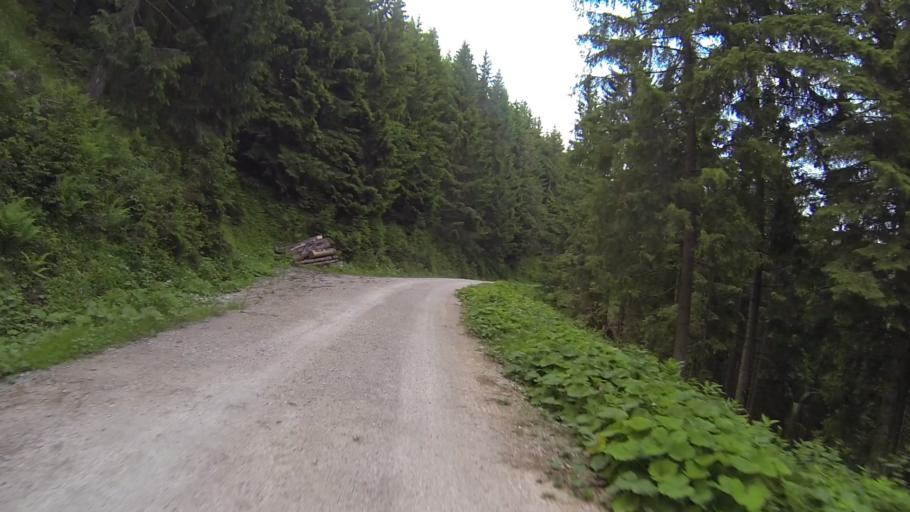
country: AT
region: Tyrol
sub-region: Politischer Bezirk Reutte
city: Jungholz
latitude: 47.5822
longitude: 10.4826
